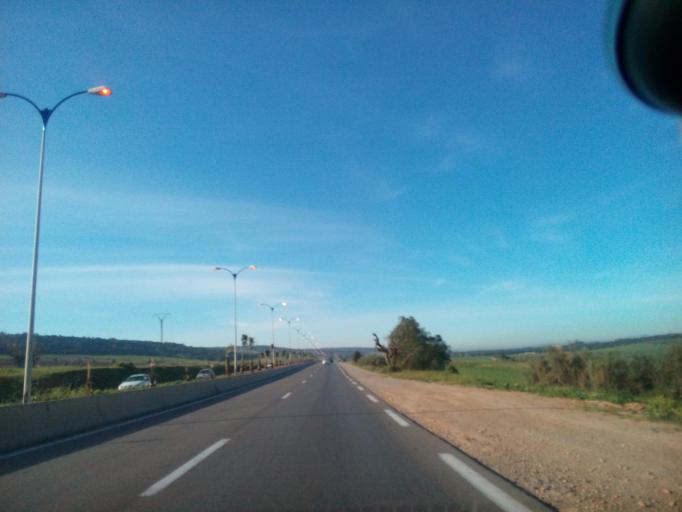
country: DZ
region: Mostaganem
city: Mostaganem
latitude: 35.8194
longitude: -0.0205
